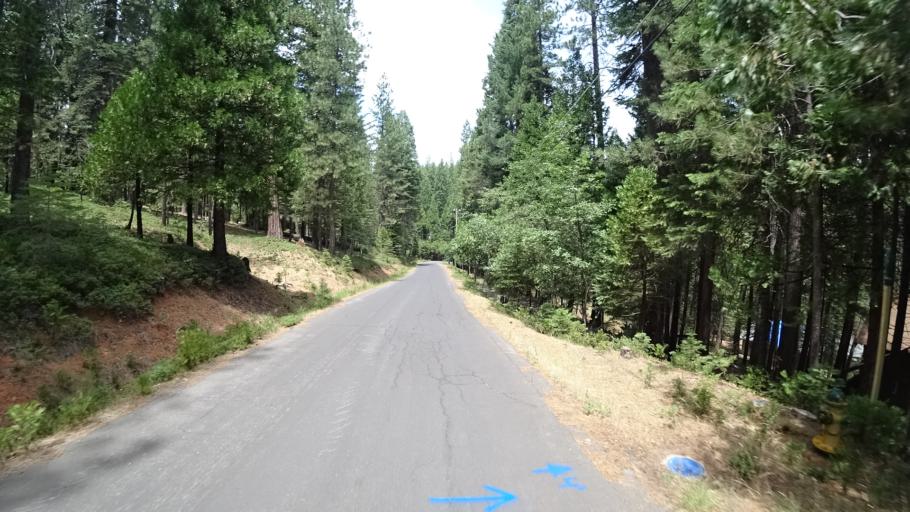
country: US
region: California
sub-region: Calaveras County
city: Arnold
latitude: 38.2378
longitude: -120.3442
